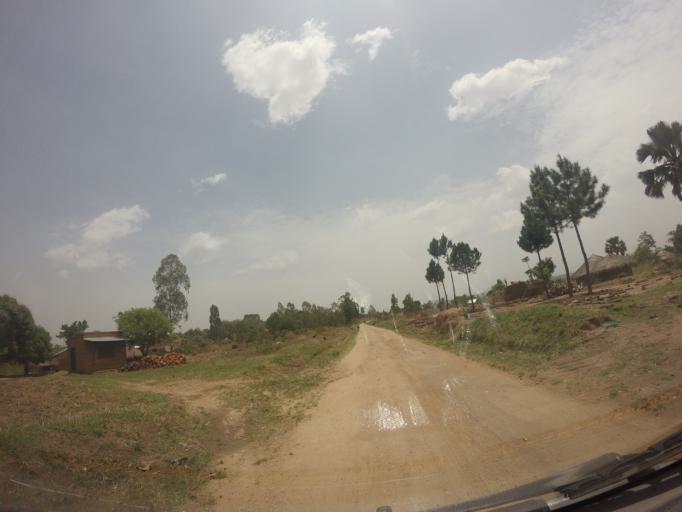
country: UG
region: Northern Region
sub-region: Arua District
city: Arua
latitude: 2.9418
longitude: 30.9140
